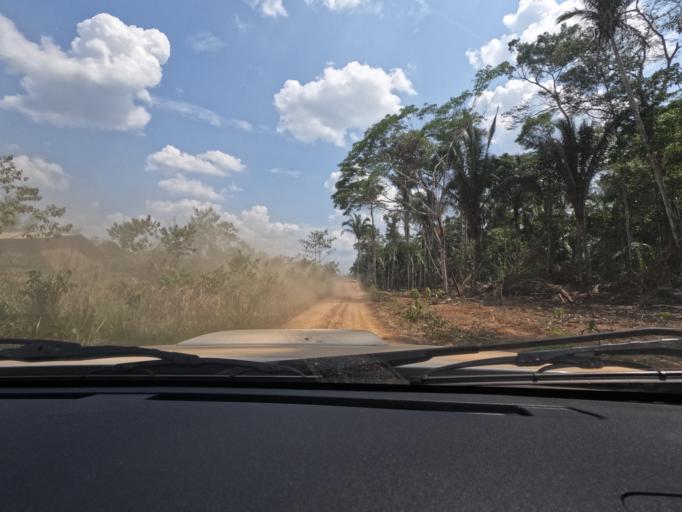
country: BR
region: Rondonia
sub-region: Porto Velho
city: Porto Velho
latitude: -8.6051
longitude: -64.2199
